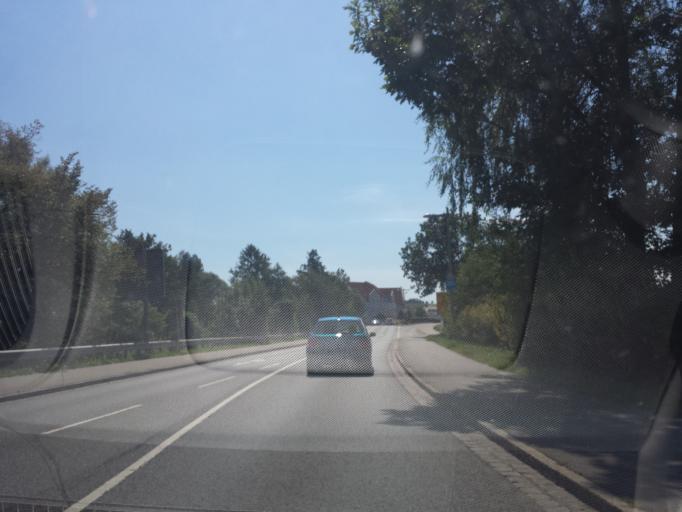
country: DE
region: Bavaria
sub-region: Upper Palatinate
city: Cham
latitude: 49.2106
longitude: 12.6684
